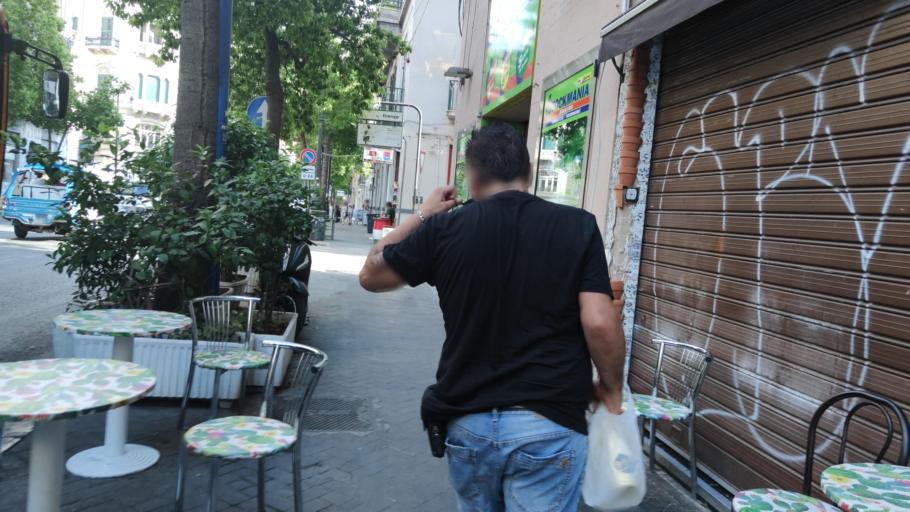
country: IT
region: Sicily
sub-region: Palermo
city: Palermo
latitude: 38.1160
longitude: 13.3639
